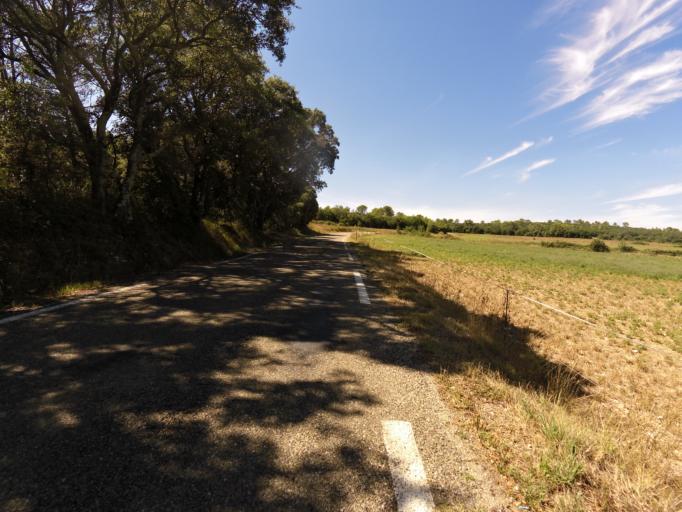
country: FR
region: Languedoc-Roussillon
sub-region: Departement du Gard
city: Sommieres
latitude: 43.8460
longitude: 4.0543
